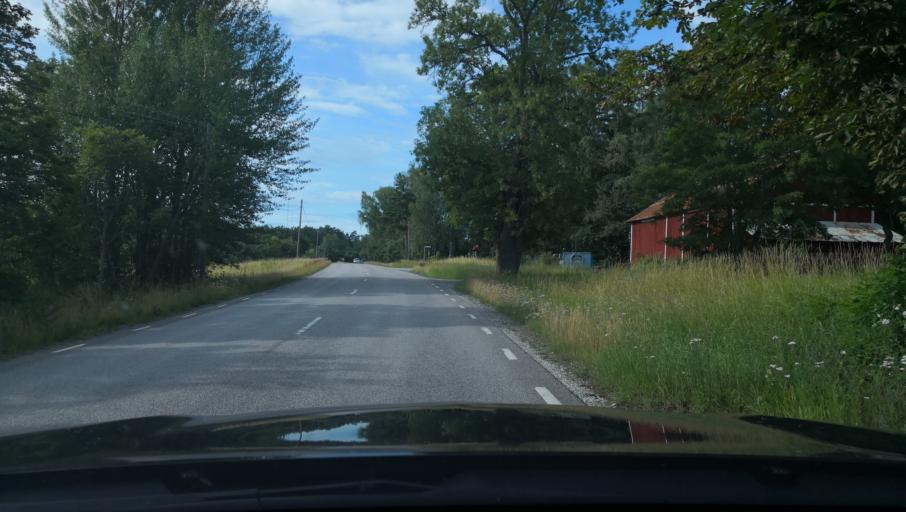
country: SE
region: Uppsala
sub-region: Habo Kommun
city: Balsta
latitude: 59.5994
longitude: 17.5088
